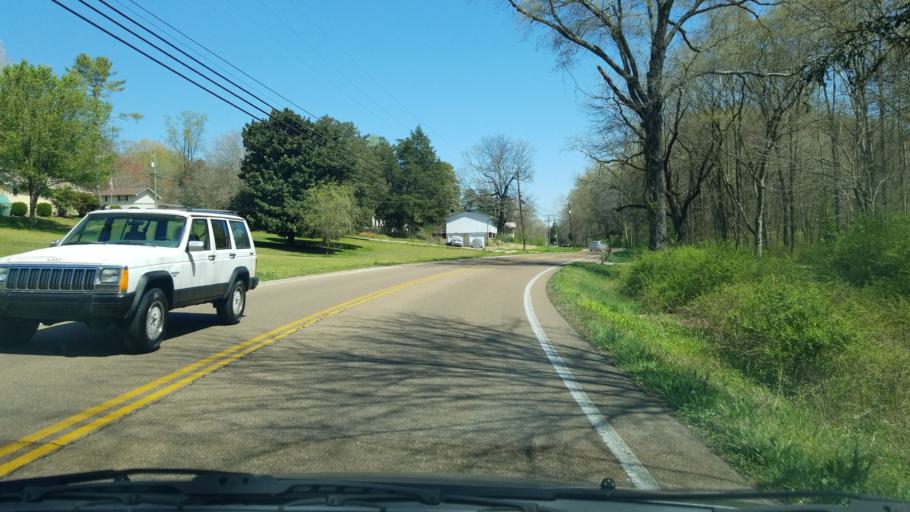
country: US
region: Tennessee
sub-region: Hamilton County
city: Middle Valley
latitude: 35.1768
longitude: -85.2026
